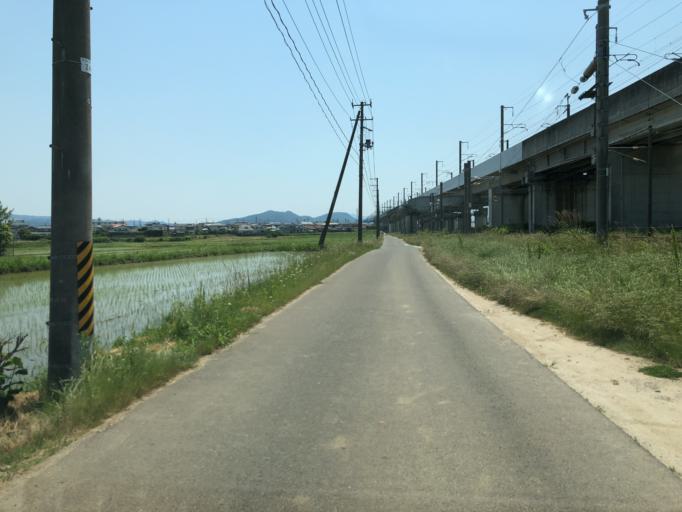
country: JP
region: Fukushima
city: Hobaramachi
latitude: 37.8302
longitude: 140.4981
